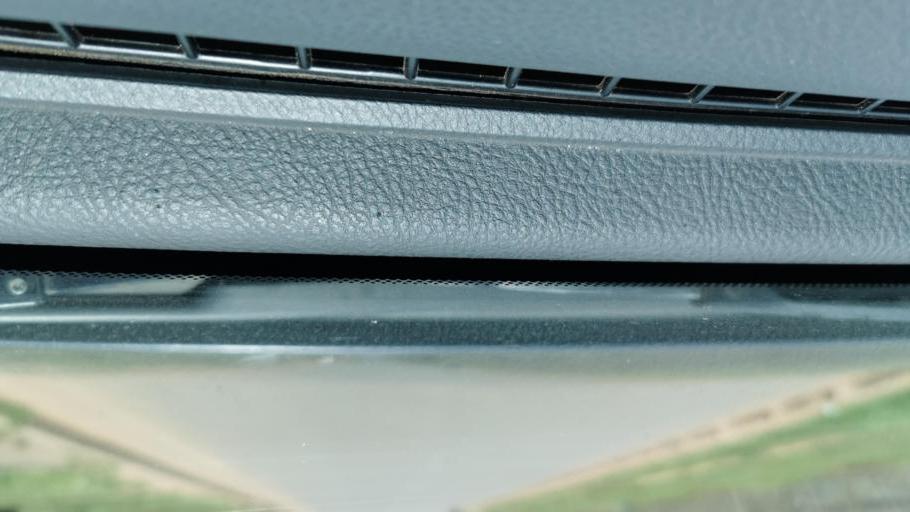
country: TG
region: Maritime
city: Lome
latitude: 6.2122
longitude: 1.1964
